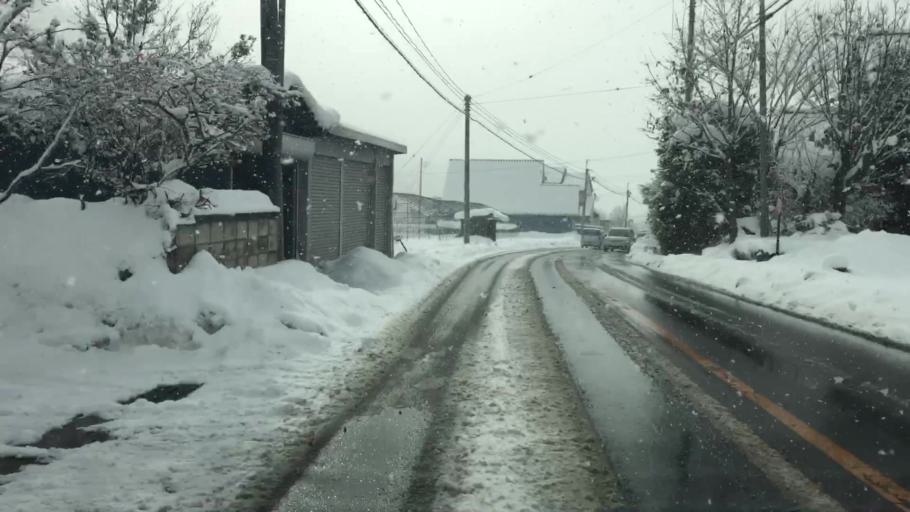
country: JP
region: Gunma
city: Numata
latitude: 36.7046
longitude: 139.0657
